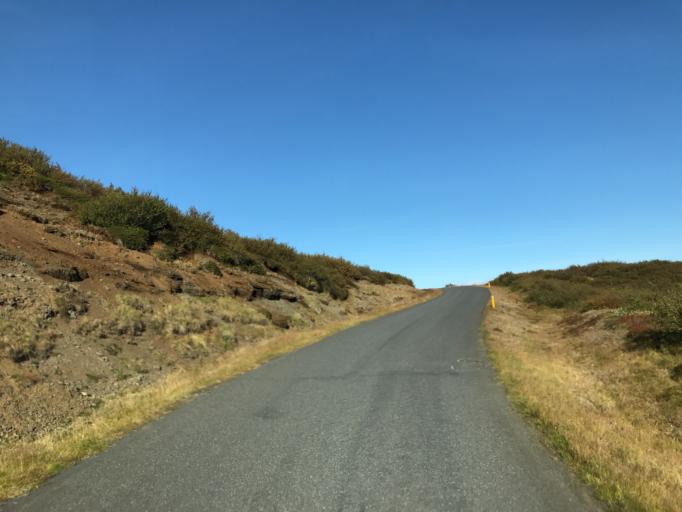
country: IS
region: South
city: Hveragerdi
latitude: 64.1568
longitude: -21.2524
